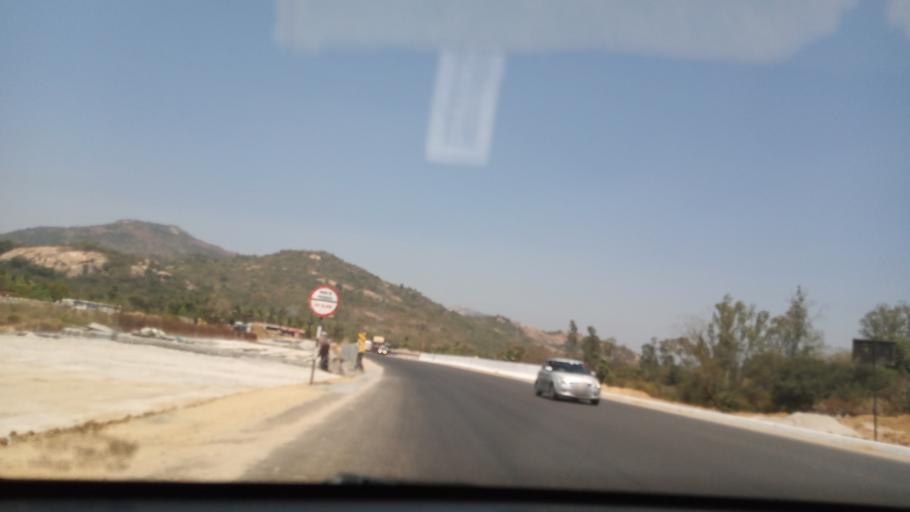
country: IN
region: Andhra Pradesh
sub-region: Chittoor
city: Pakala
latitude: 13.4702
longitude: 79.1799
